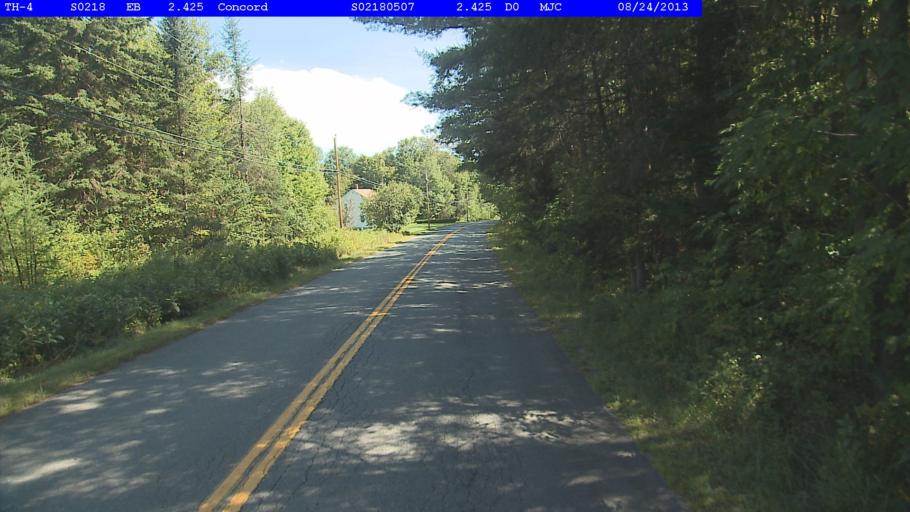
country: US
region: New Hampshire
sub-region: Grafton County
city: Littleton
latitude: 44.4335
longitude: -71.7553
